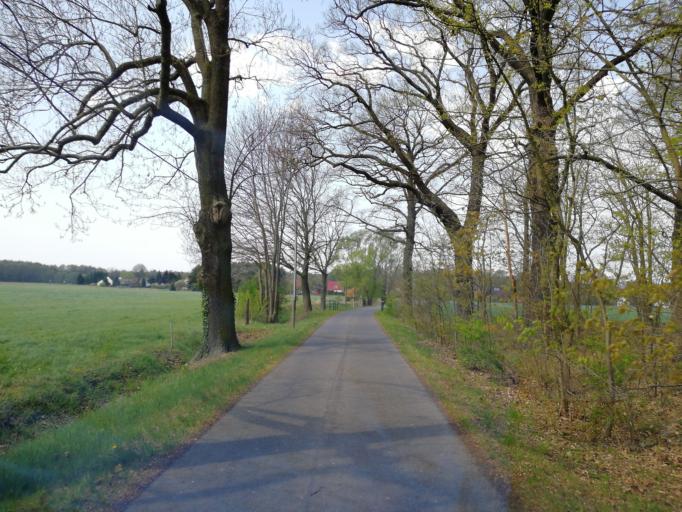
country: DE
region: Brandenburg
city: Crinitz
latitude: 51.7369
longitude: 13.8557
